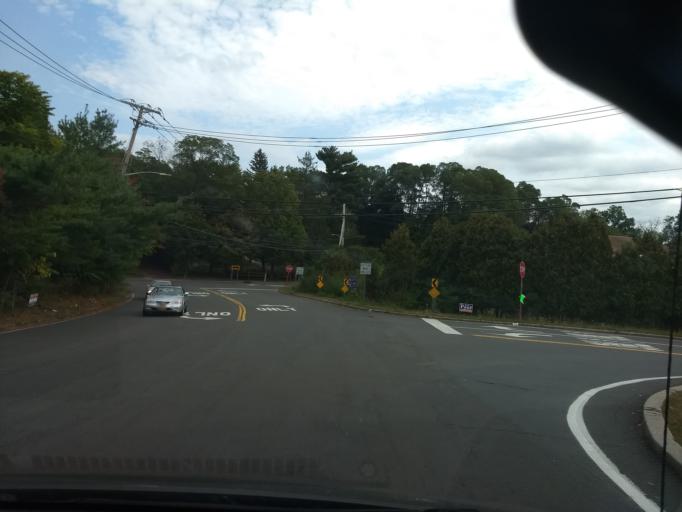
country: US
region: New York
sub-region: Rockland County
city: Chestnut Ridge
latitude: 41.0898
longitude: -74.0355
